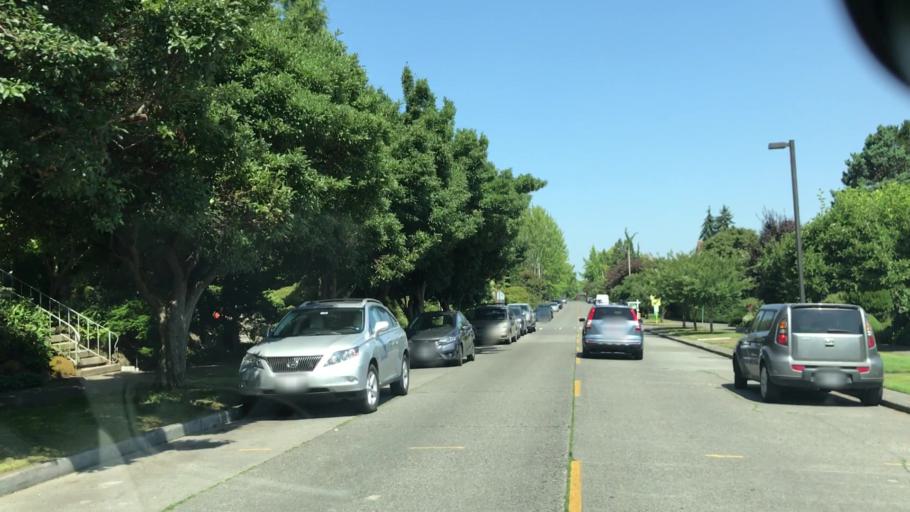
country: US
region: Washington
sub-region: King County
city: Medina
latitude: 47.6303
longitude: -122.2814
